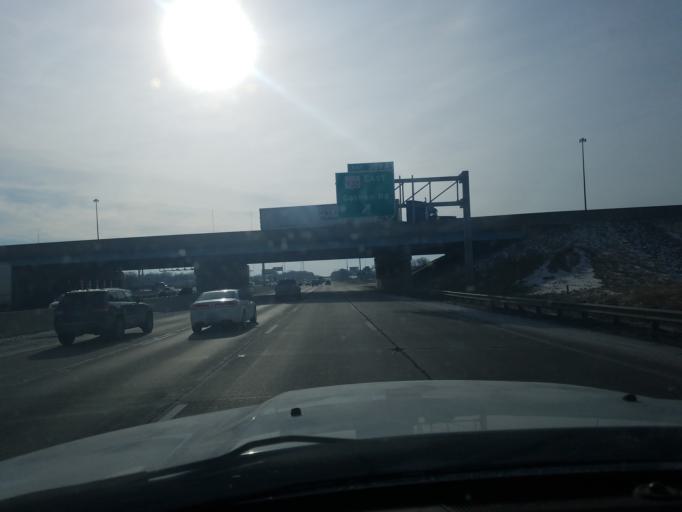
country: US
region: Indiana
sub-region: Allen County
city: Fort Wayne
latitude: 41.1228
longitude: -85.1863
